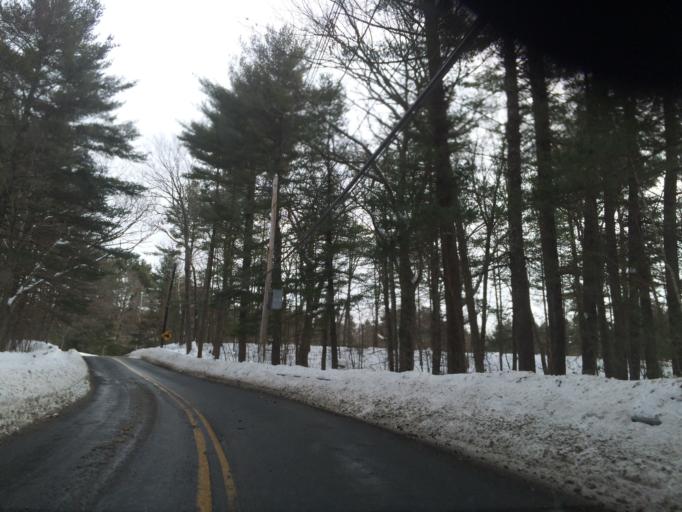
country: US
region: Massachusetts
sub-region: Middlesex County
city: Weston
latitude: 42.3794
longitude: -71.3169
